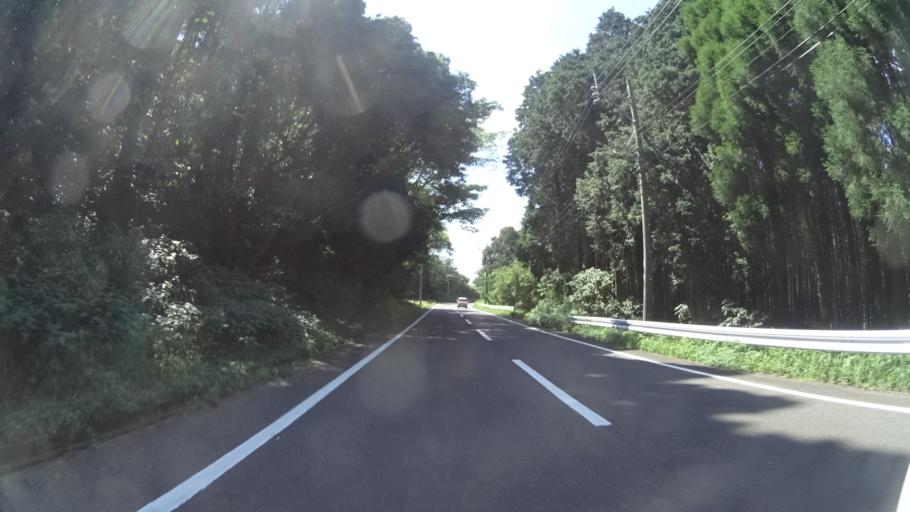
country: JP
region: Kagoshima
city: Kokubu-matsuki
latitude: 31.8200
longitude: 130.7175
